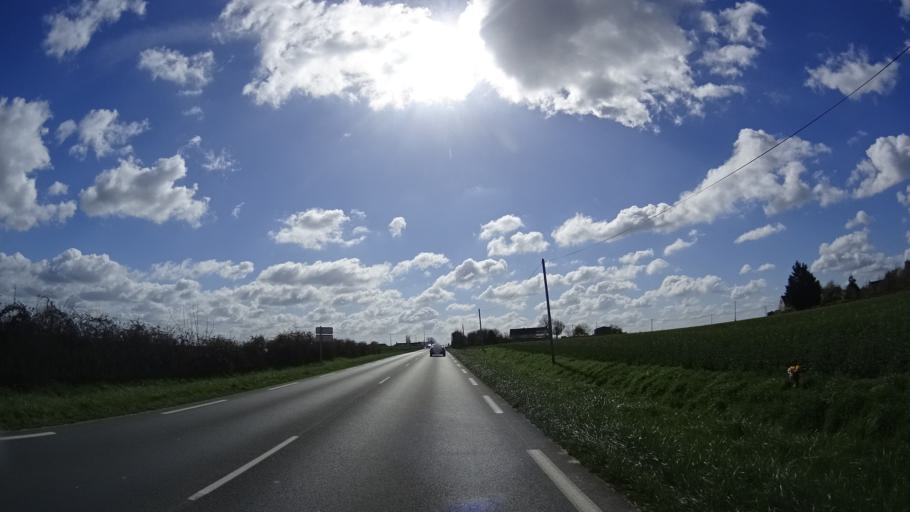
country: FR
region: Pays de la Loire
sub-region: Departement de Maine-et-Loire
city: Brissac-Quince
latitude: 47.3290
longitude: -0.4201
